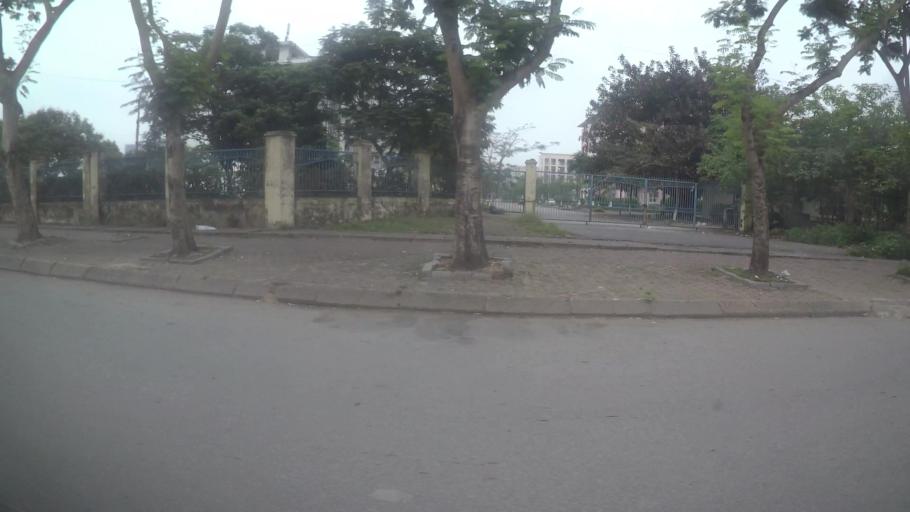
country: VN
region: Ha Noi
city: Cau Dien
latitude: 21.0250
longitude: 105.7634
